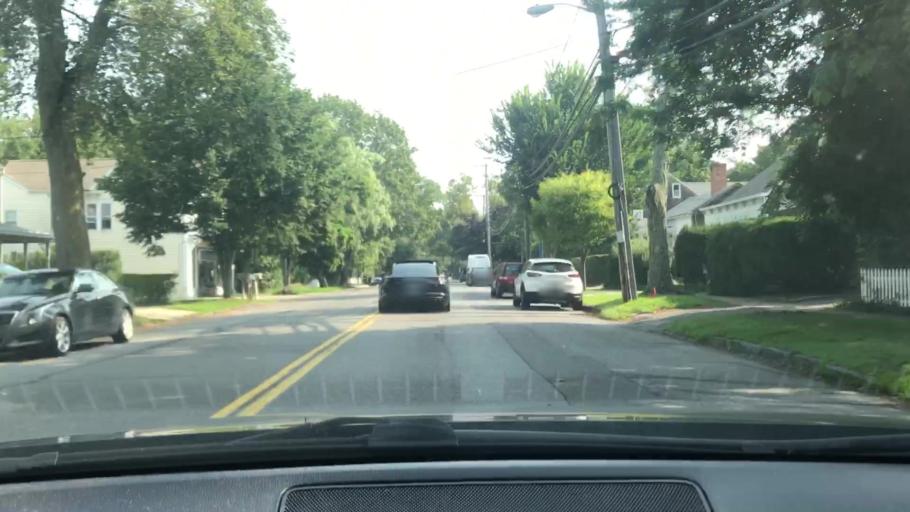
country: US
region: New York
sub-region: Suffolk County
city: Sag Harbor
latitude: 40.9937
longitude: -72.2998
